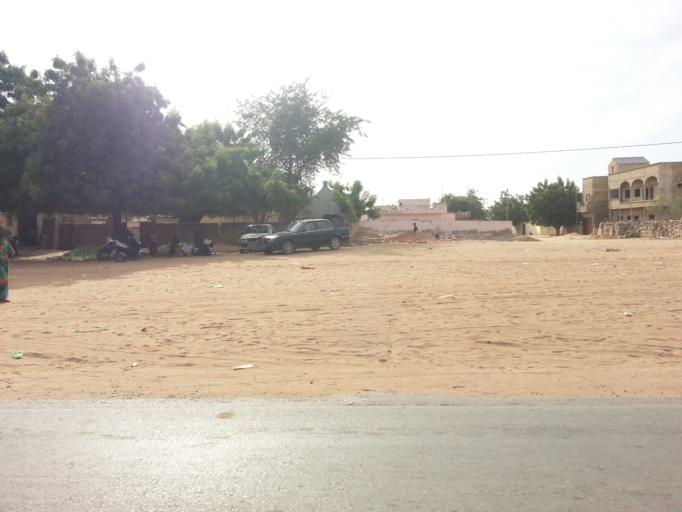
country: SN
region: Diourbel
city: Touba
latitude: 14.8709
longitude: -15.8628
